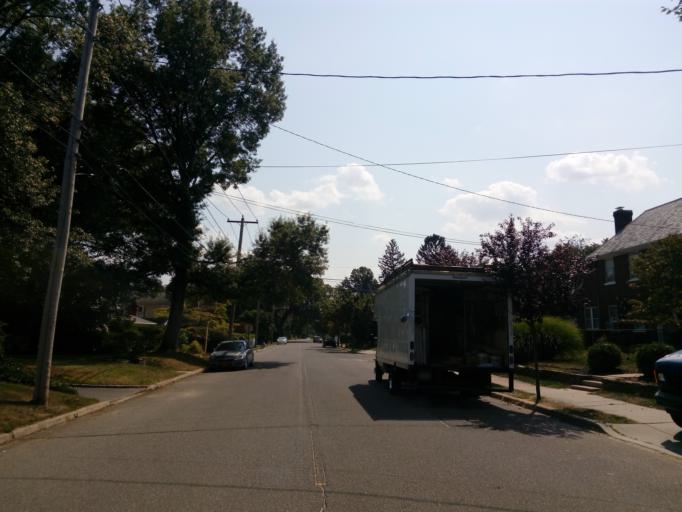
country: US
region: New York
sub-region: Nassau County
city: Locust Valley
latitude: 40.8815
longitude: -73.5931
